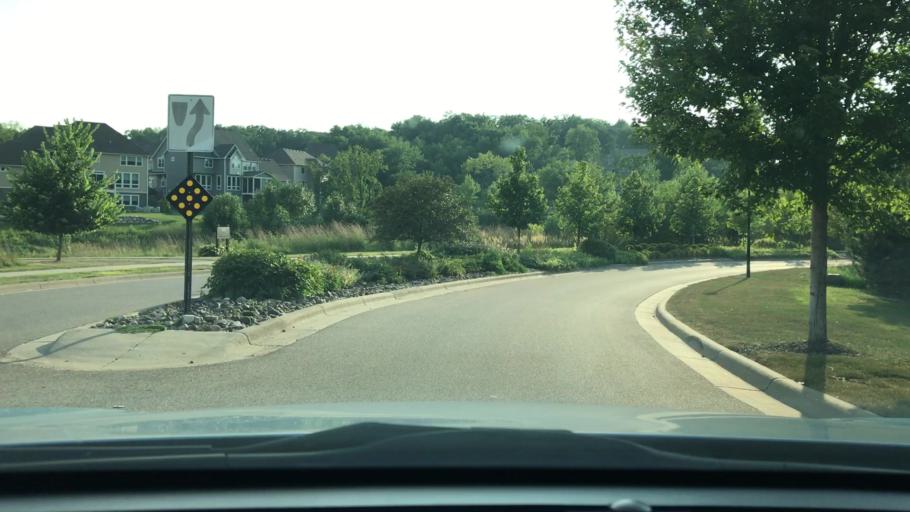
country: US
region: Minnesota
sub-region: Hennepin County
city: Maple Grove
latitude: 45.0533
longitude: -93.4750
